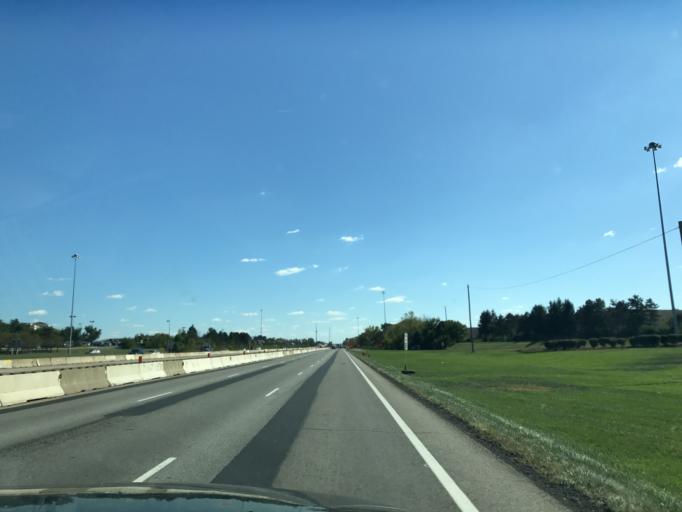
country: US
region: Ohio
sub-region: Franklin County
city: Dublin
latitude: 40.0751
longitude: -83.1357
